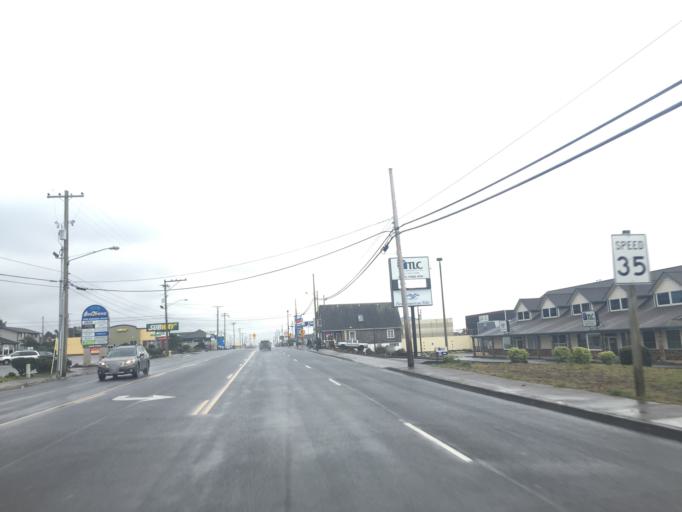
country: US
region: Oregon
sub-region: Lincoln County
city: Newport
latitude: 44.6501
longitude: -124.0531
